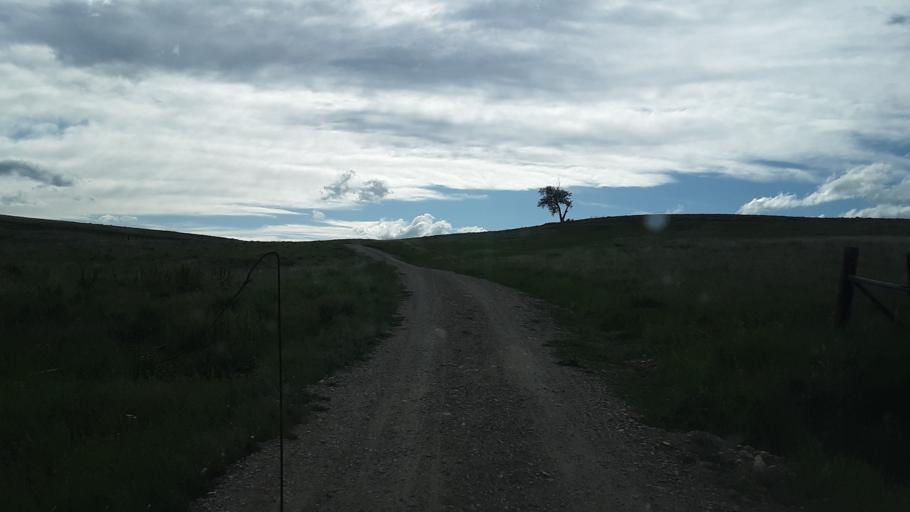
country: US
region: Montana
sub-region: Carbon County
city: Red Lodge
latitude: 45.3712
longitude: -109.1860
